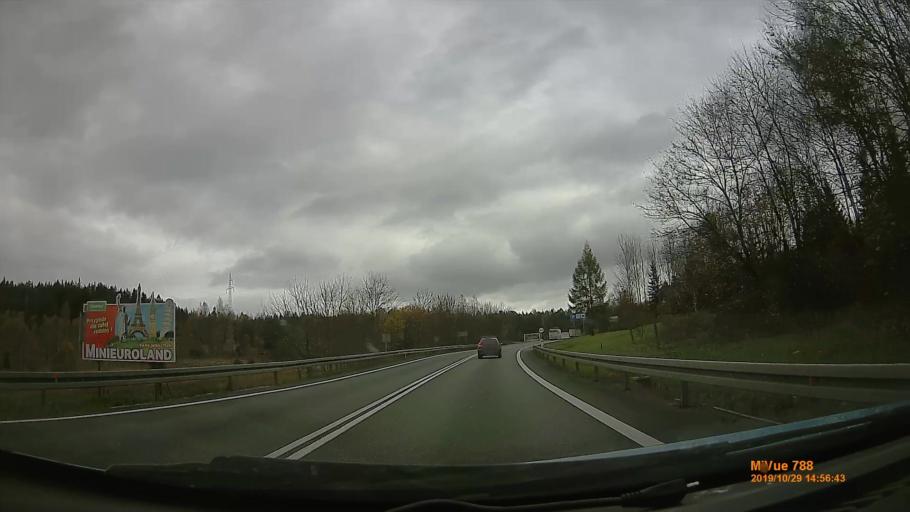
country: PL
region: Lower Silesian Voivodeship
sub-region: Powiat klodzki
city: Szczytna
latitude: 50.4225
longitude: 16.4575
